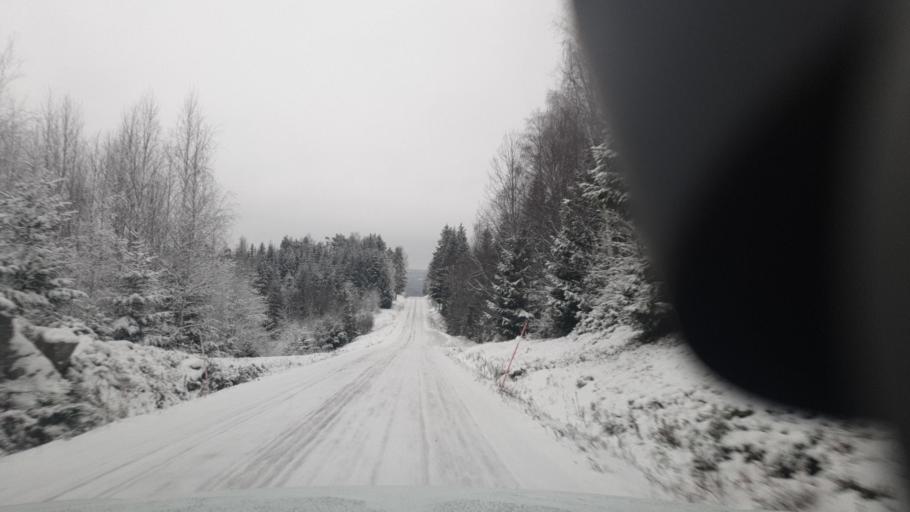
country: NO
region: Ostfold
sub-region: Romskog
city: Romskog
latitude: 59.7196
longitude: 12.0687
